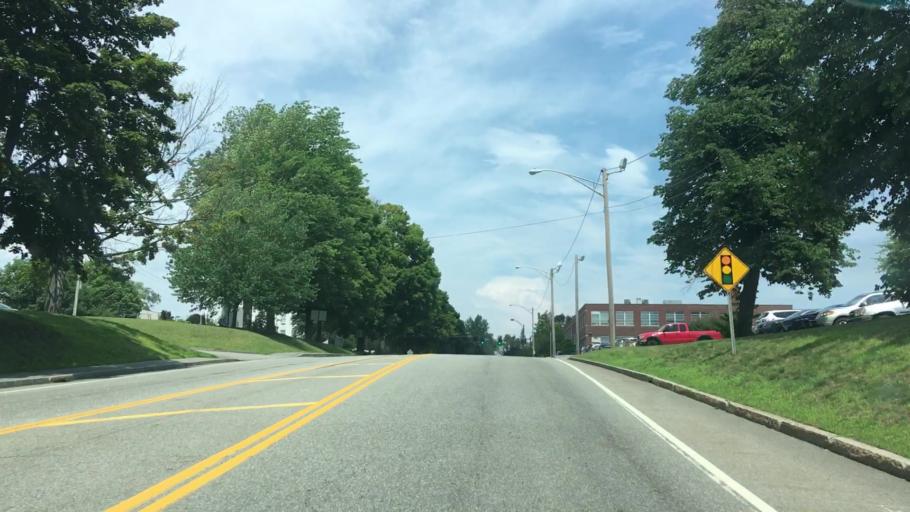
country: US
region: Maine
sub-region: Kennebec County
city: Augusta
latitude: 44.3042
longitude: -69.7816
